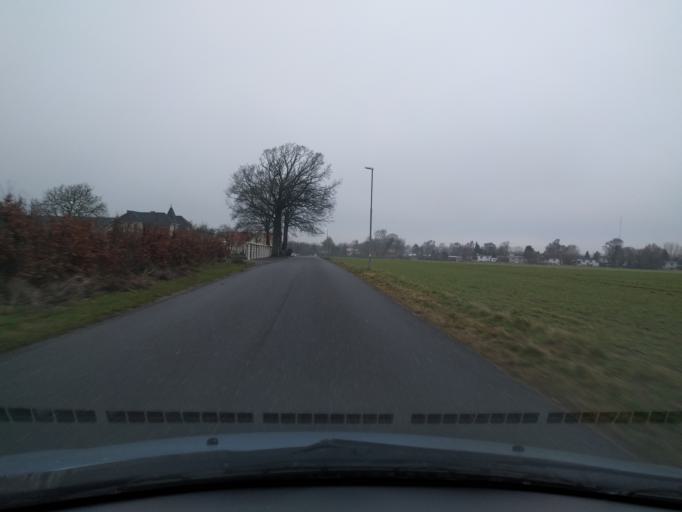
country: DK
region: South Denmark
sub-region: Odense Kommune
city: Bullerup
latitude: 55.4016
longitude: 10.5110
